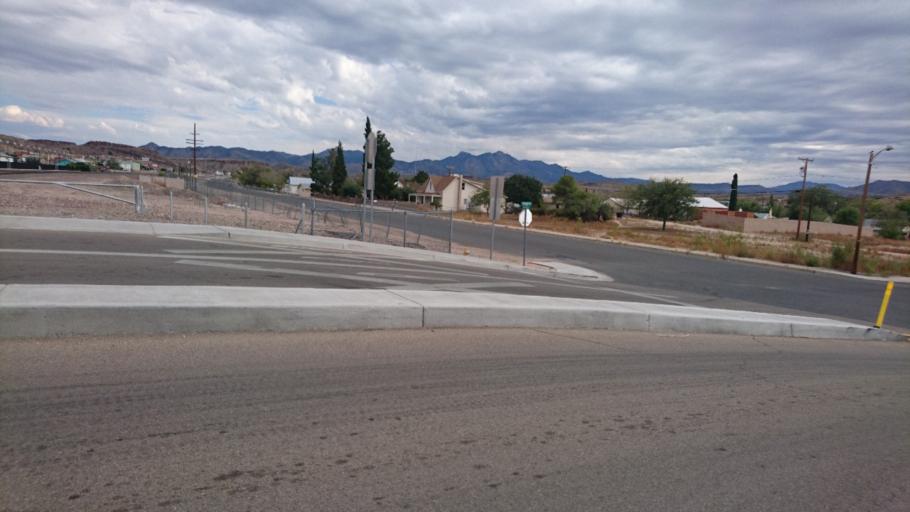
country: US
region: Arizona
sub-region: Mohave County
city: Kingman
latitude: 35.1880
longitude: -114.0532
